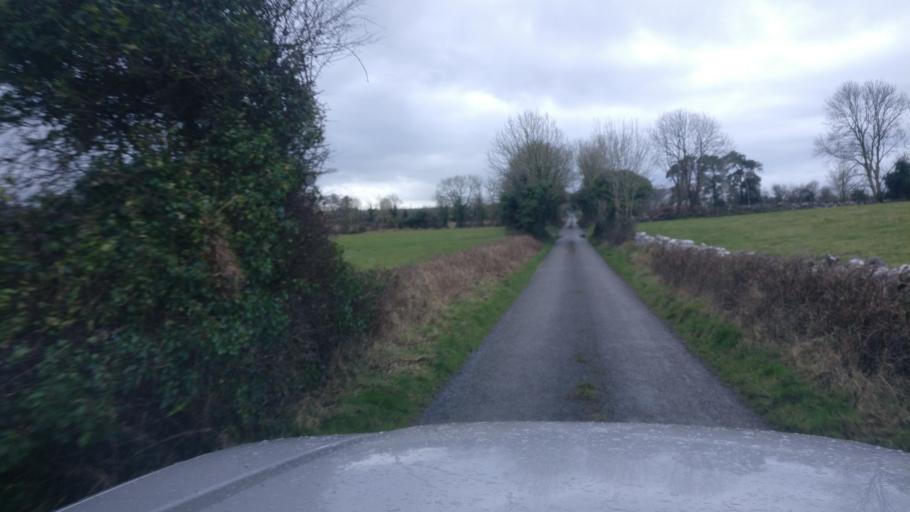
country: IE
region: Connaught
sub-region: County Galway
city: Athenry
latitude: 53.1925
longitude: -8.6880
